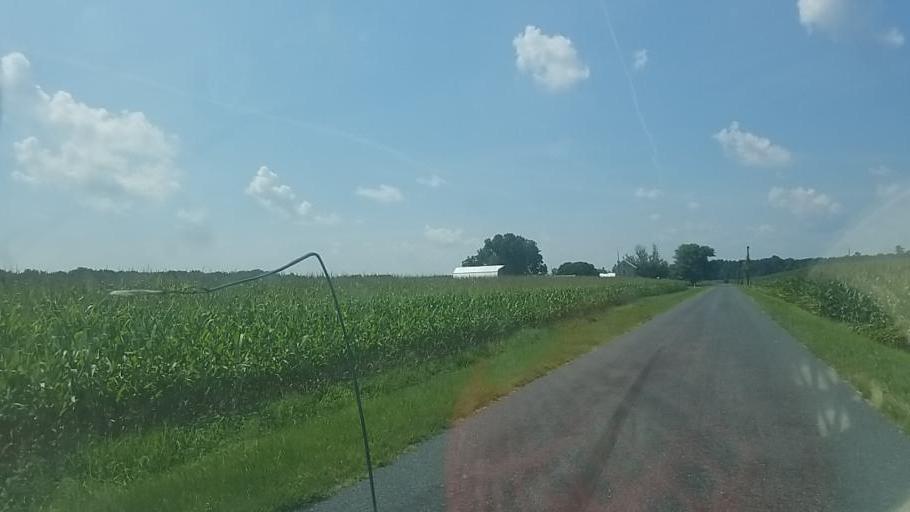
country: US
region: Maryland
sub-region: Worcester County
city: Berlin
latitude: 38.2967
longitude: -75.2920
